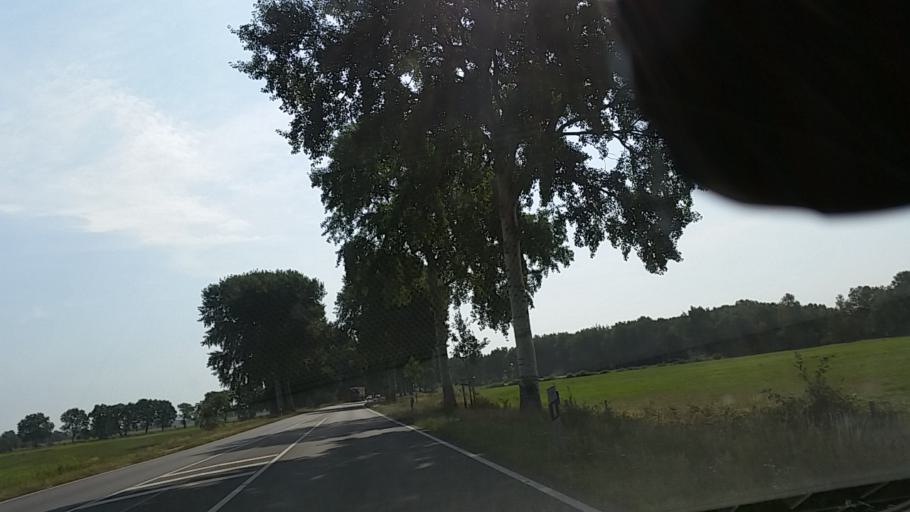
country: DE
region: Lower Saxony
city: Diepholz
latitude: 52.6139
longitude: 8.3109
